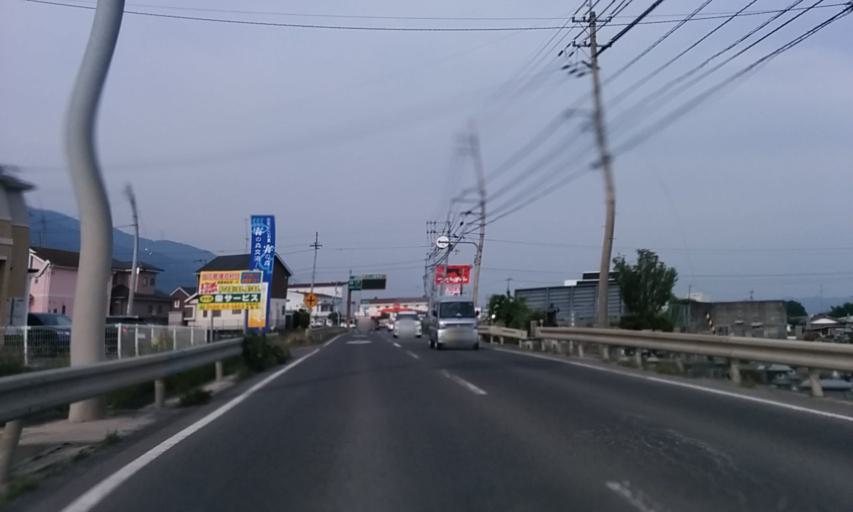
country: JP
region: Ehime
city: Kawanoecho
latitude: 33.9658
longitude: 133.4731
